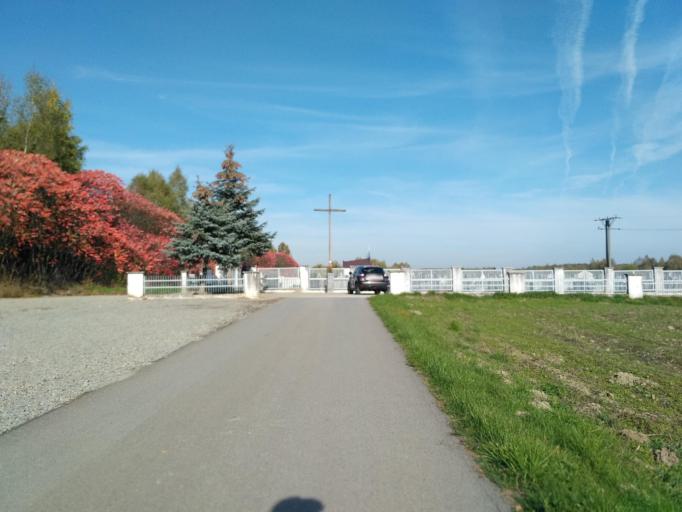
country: PL
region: Subcarpathian Voivodeship
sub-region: Powiat rzeszowski
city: Trzciana
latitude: 50.0768
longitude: 21.7926
